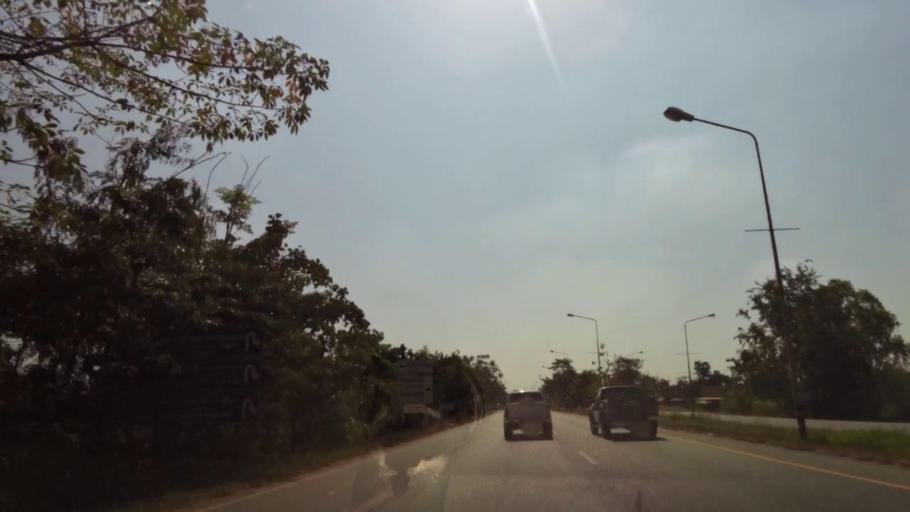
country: TH
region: Phichit
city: Wachira Barami
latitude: 16.4123
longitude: 100.1431
